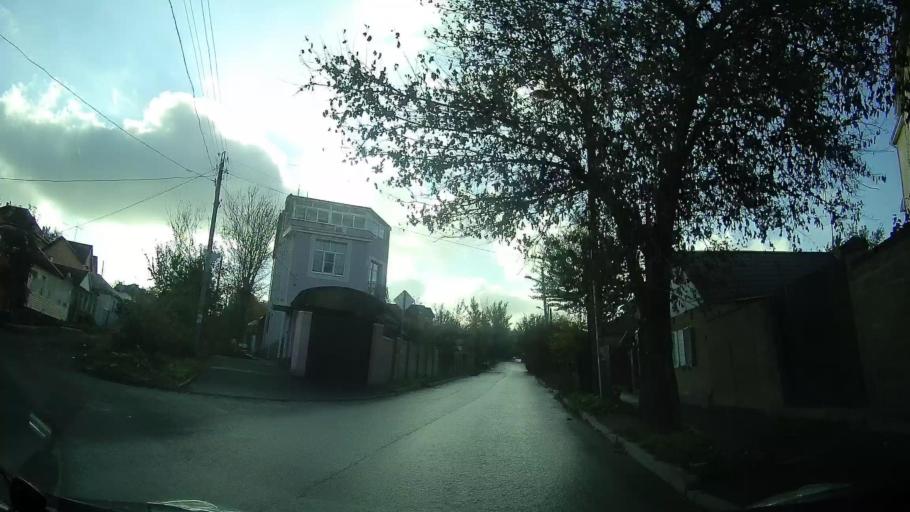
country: RU
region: Rostov
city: Severnyy
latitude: 47.2573
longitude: 39.6897
